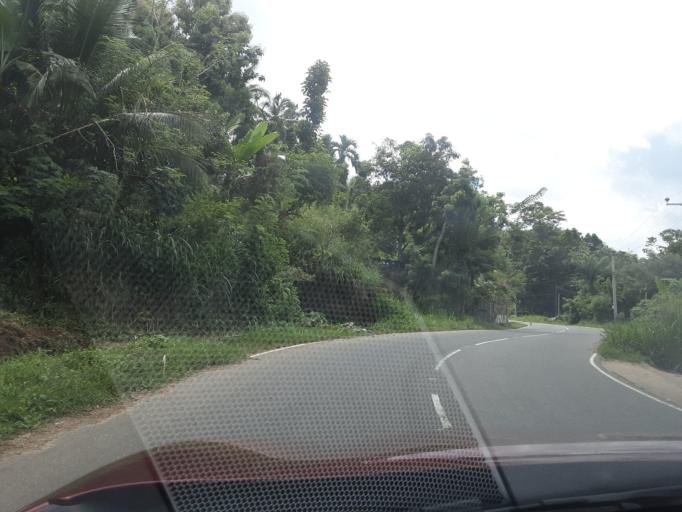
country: LK
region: Uva
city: Monaragala
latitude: 6.8966
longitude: 81.2498
